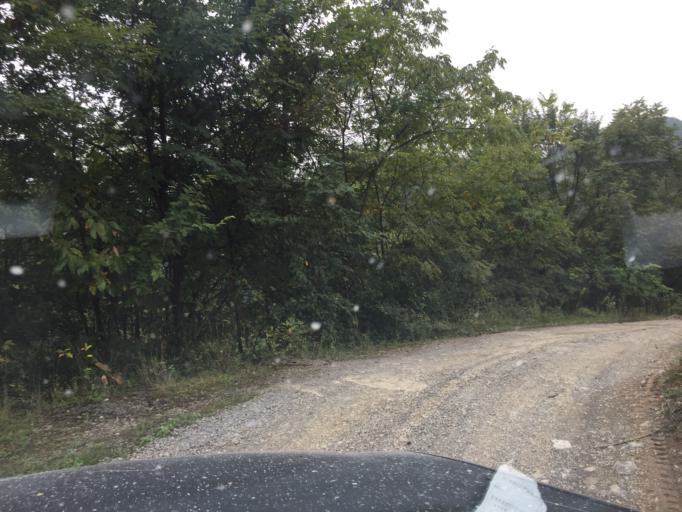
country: CN
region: Guizhou Sheng
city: Nangan
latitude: 28.2533
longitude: 107.9484
